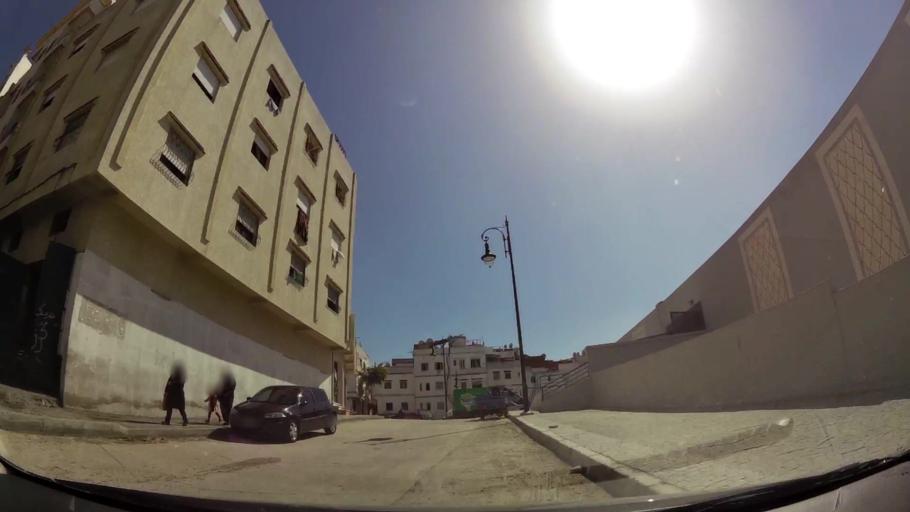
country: MA
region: Tanger-Tetouan
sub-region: Tanger-Assilah
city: Tangier
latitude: 35.7429
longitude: -5.8142
